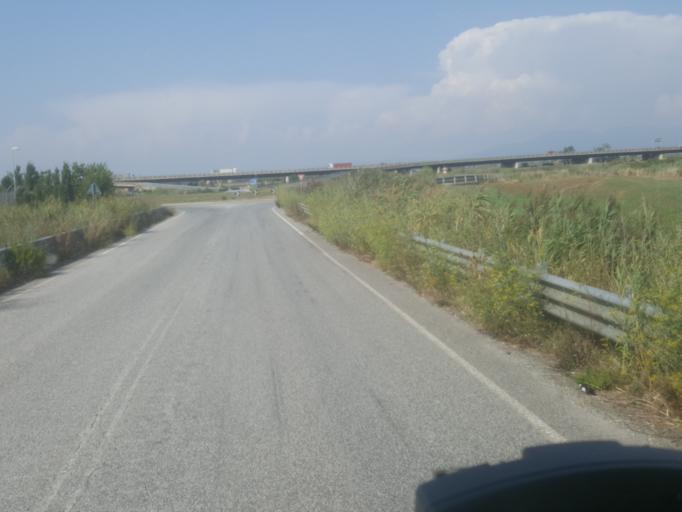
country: IT
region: Tuscany
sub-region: Provincia di Livorno
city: Guasticce
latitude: 43.6055
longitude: 10.4078
